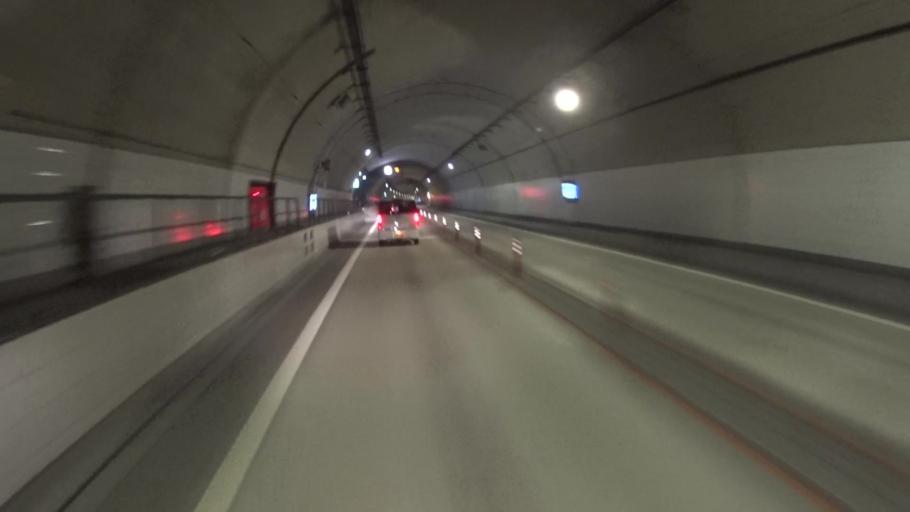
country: JP
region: Kyoto
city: Miyazu
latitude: 35.5254
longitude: 135.1776
